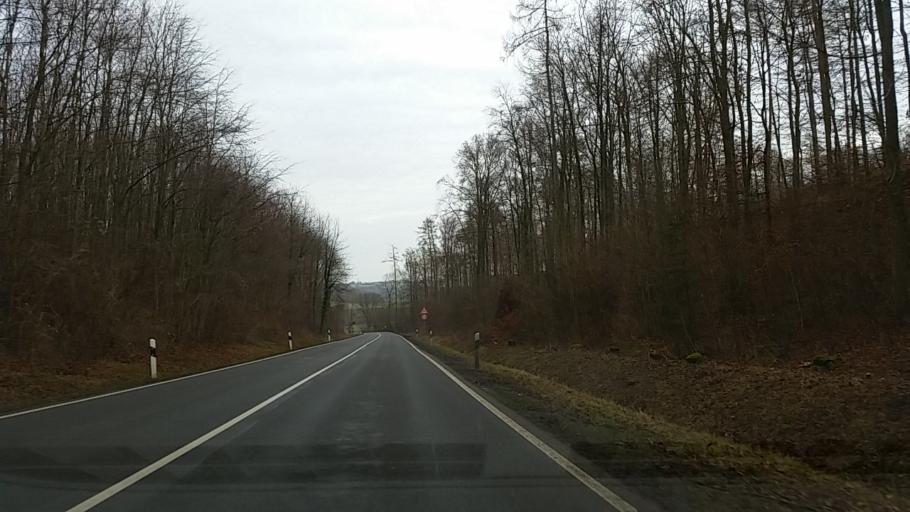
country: DE
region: Lower Saxony
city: Alt Wallmoden
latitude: 52.0151
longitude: 10.3131
